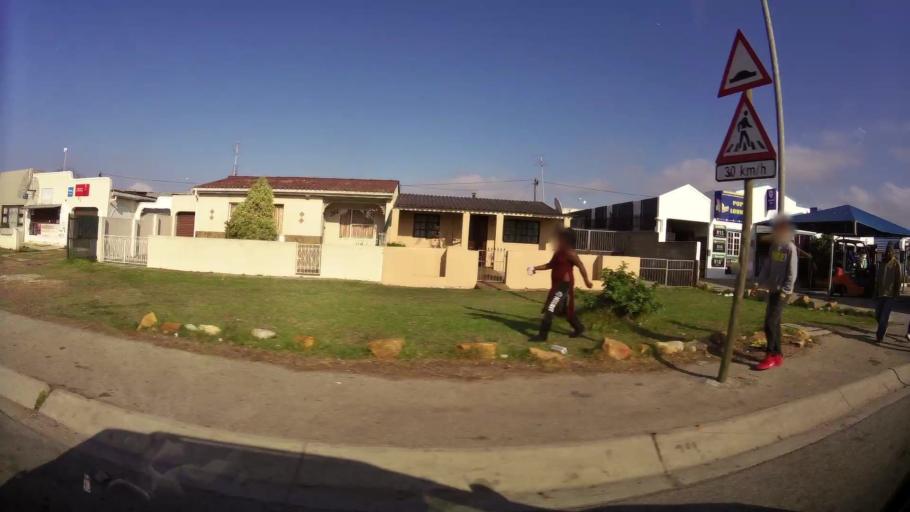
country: ZA
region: Eastern Cape
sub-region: Nelson Mandela Bay Metropolitan Municipality
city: Port Elizabeth
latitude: -33.9225
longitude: 25.5327
